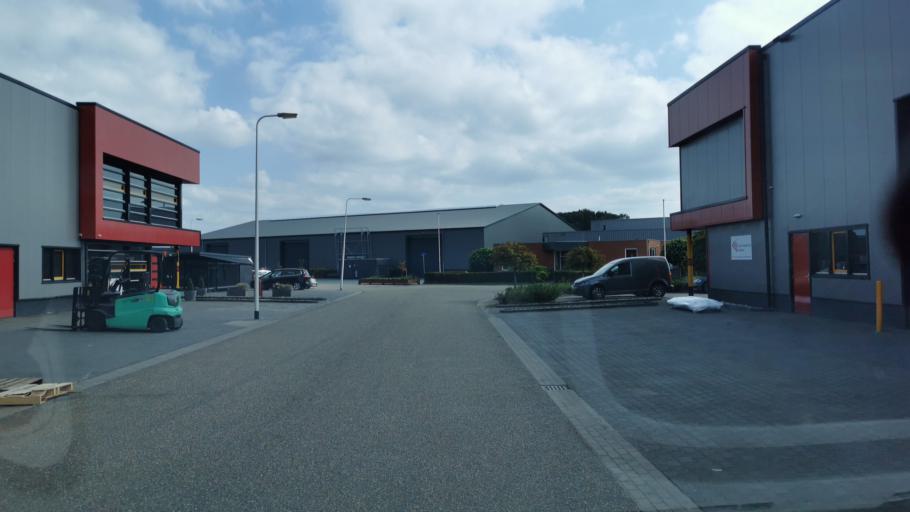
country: NL
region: Overijssel
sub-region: Gemeente Oldenzaal
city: Oldenzaal
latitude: 52.3439
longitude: 6.8564
